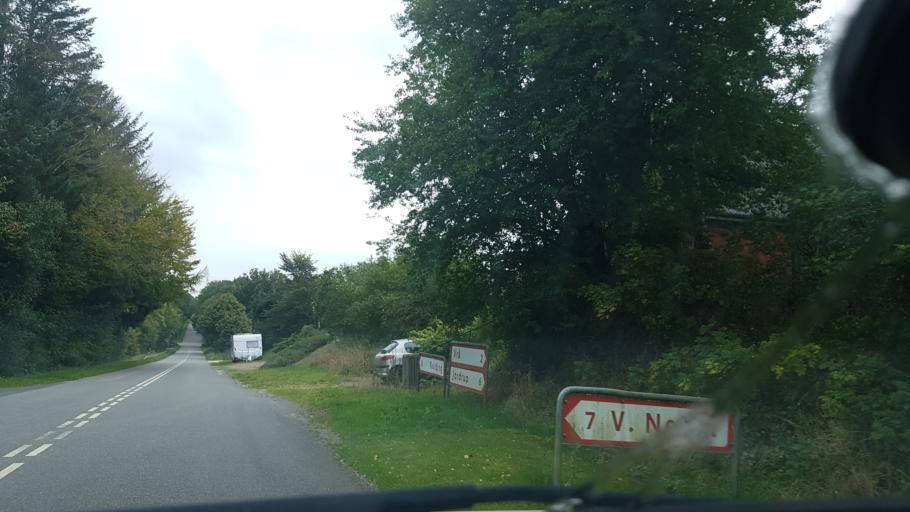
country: DK
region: South Denmark
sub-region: Kolding Kommune
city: Lunderskov
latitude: 55.5138
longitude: 9.3658
